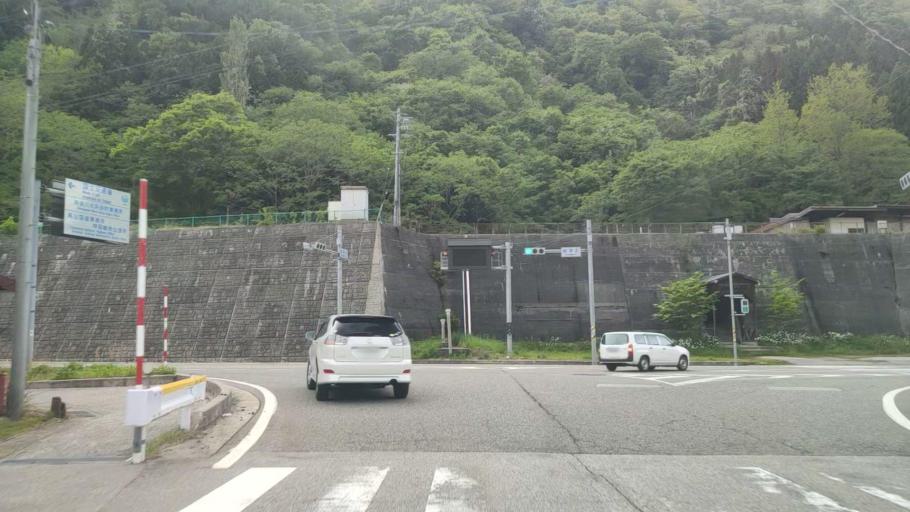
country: JP
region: Gifu
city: Takayama
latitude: 36.3403
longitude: 137.2953
